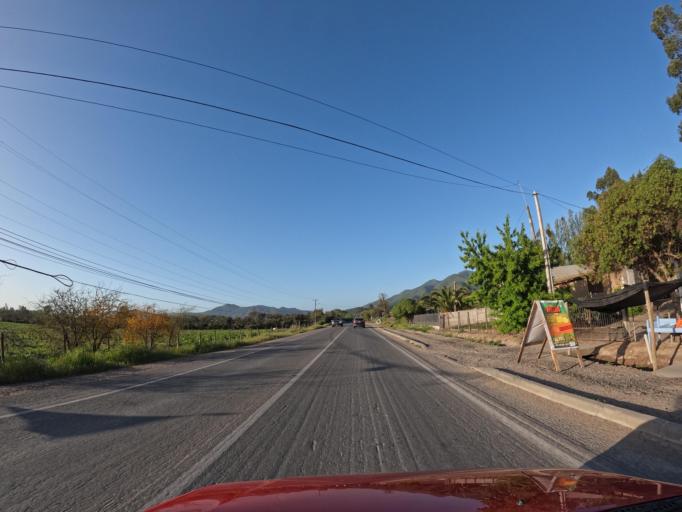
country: CL
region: O'Higgins
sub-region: Provincia de Colchagua
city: Santa Cruz
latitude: -34.4055
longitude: -71.3713
